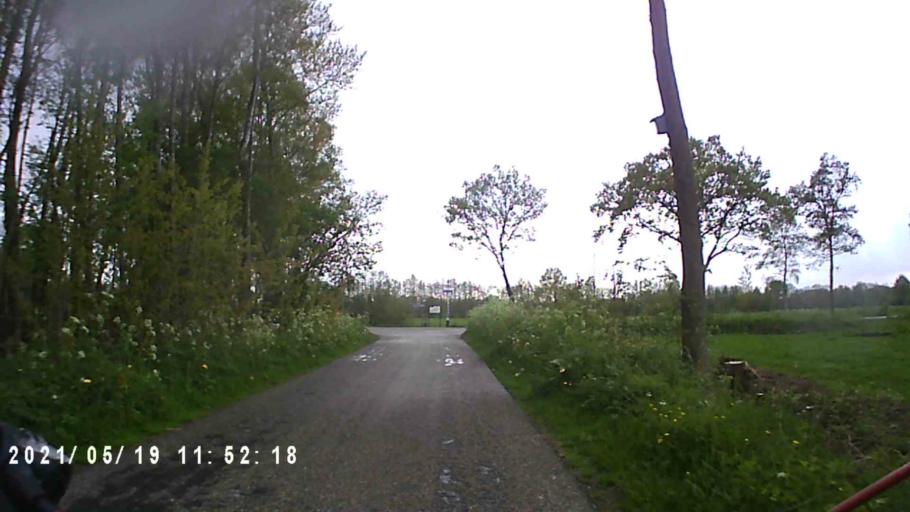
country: NL
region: Friesland
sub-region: Gemeente Achtkarspelen
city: Buitenpost
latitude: 53.2662
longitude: 6.1422
